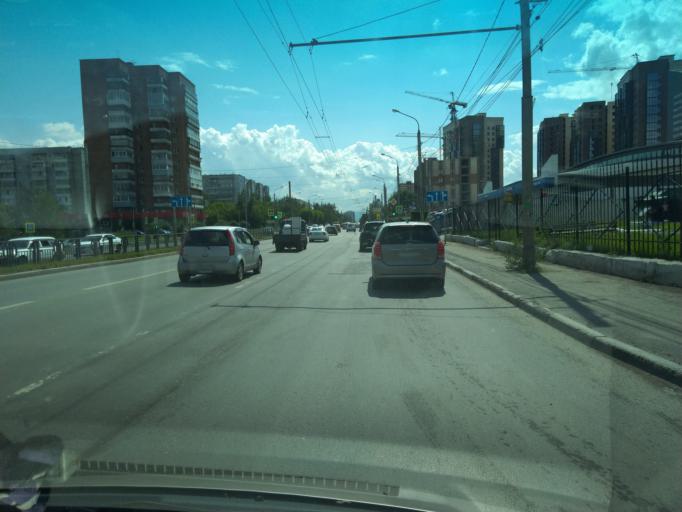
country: RU
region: Krasnoyarskiy
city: Solnechnyy
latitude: 56.0553
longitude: 92.9412
